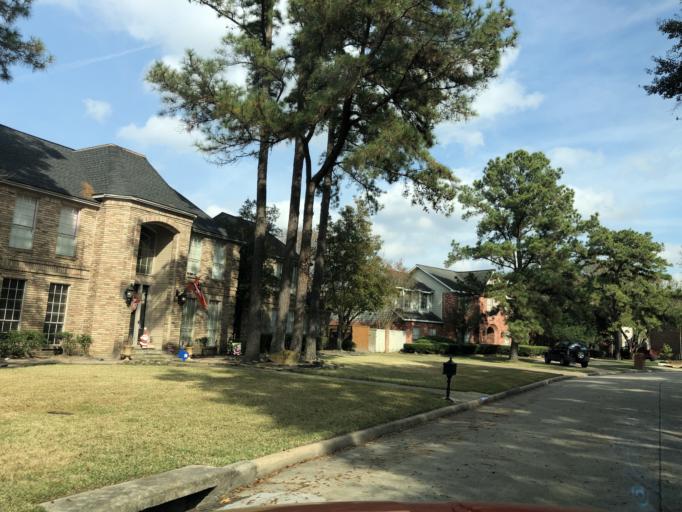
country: US
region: Texas
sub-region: Harris County
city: Tomball
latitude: 30.0213
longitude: -95.5468
